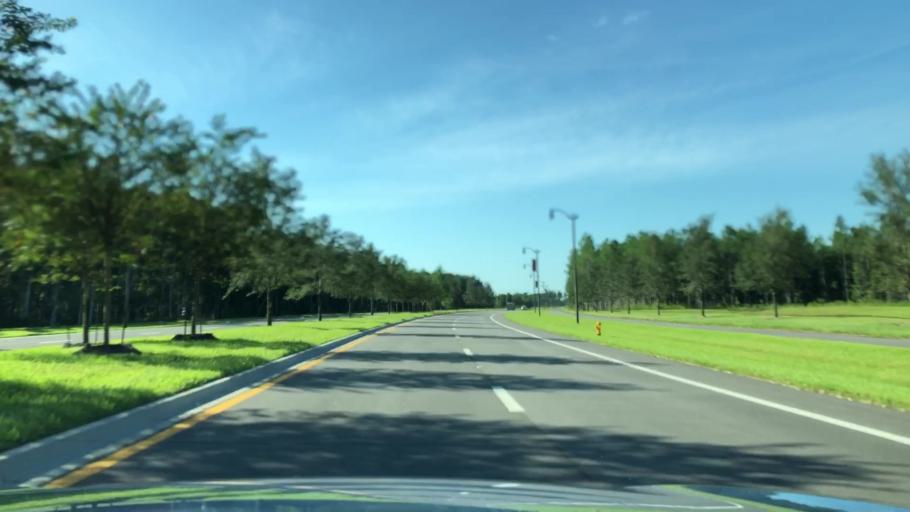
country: US
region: Florida
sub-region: Saint Johns County
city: Palm Valley
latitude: 30.0806
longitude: -81.4028
